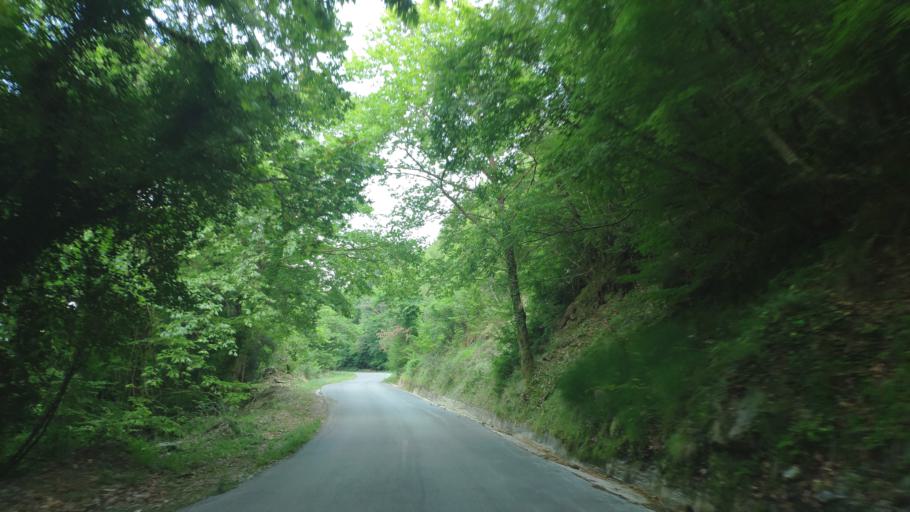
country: GR
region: Epirus
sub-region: Nomos Artas
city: Agios Dimitrios
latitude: 39.3892
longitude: 21.0206
